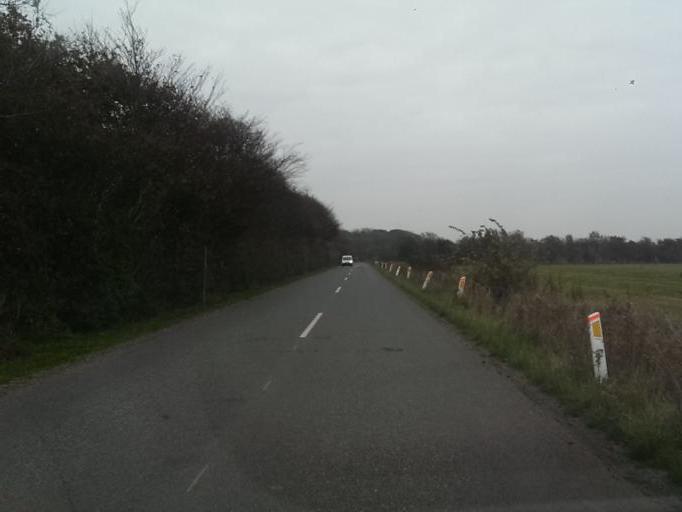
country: DK
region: South Denmark
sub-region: Esbjerg Kommune
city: Tjaereborg
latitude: 55.4985
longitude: 8.5217
